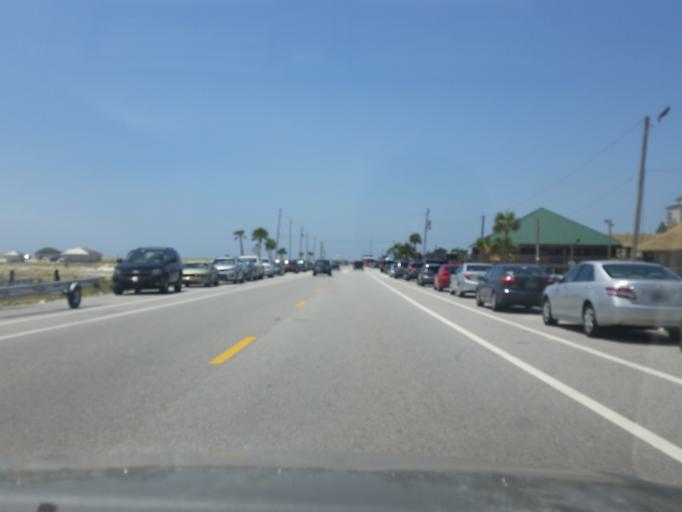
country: US
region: Florida
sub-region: Santa Rosa County
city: Navarre
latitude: 30.3849
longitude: -86.8623
